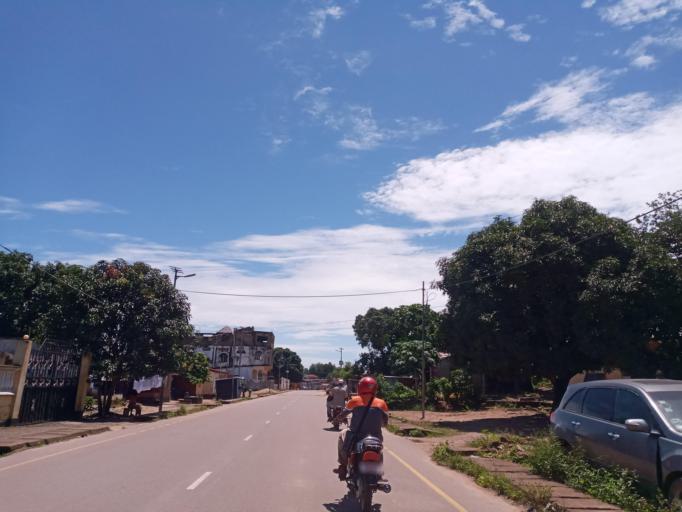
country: SL
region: Eastern Province
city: Koidu
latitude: 8.6408
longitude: -10.9755
